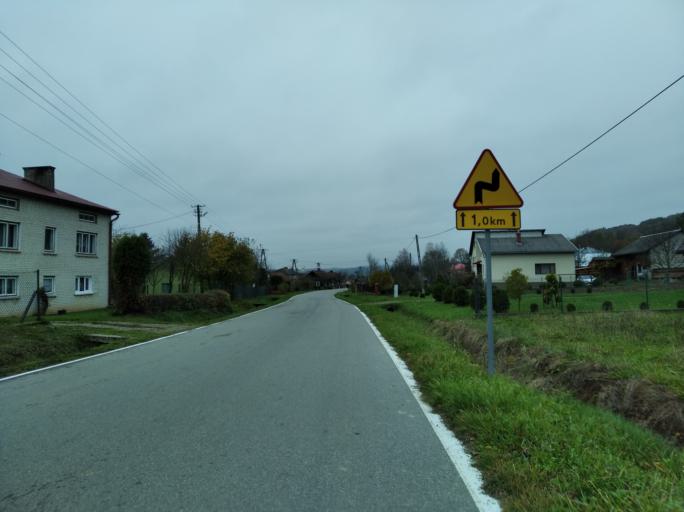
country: PL
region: Subcarpathian Voivodeship
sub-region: Powiat krosnienski
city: Leki
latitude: 49.8208
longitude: 21.6469
